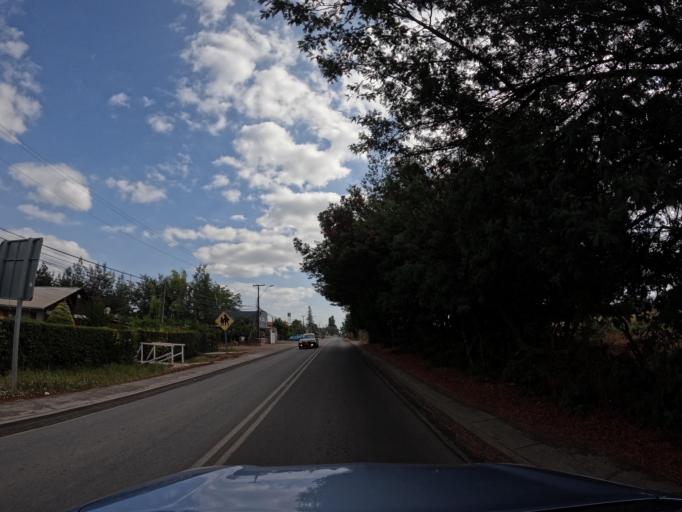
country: CL
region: Maule
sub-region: Provincia de Curico
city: Molina
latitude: -35.1598
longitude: -71.2860
